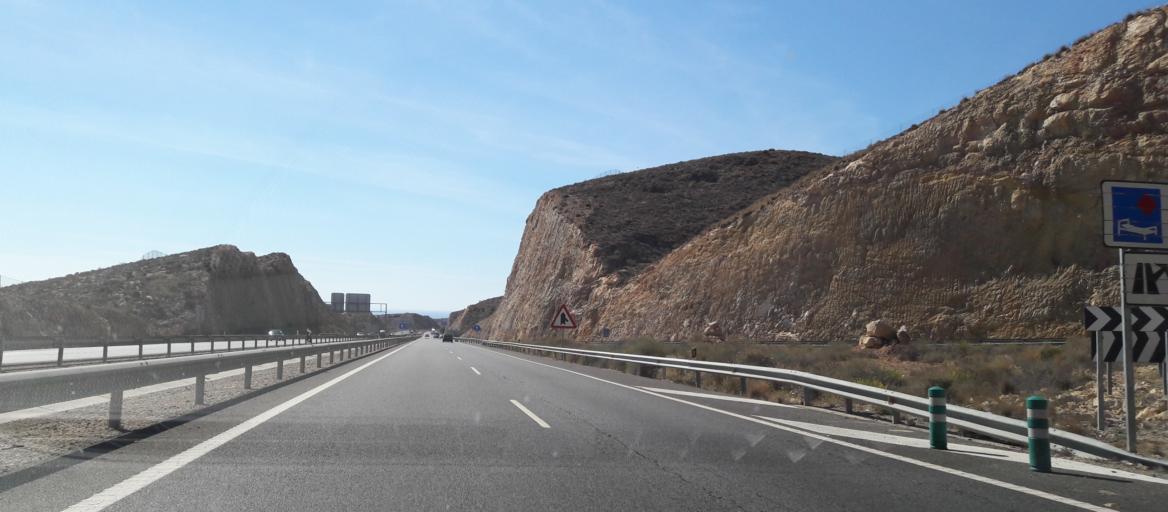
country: ES
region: Andalusia
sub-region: Provincia de Almeria
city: Huercal de Almeria
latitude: 36.8730
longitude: -2.4612
